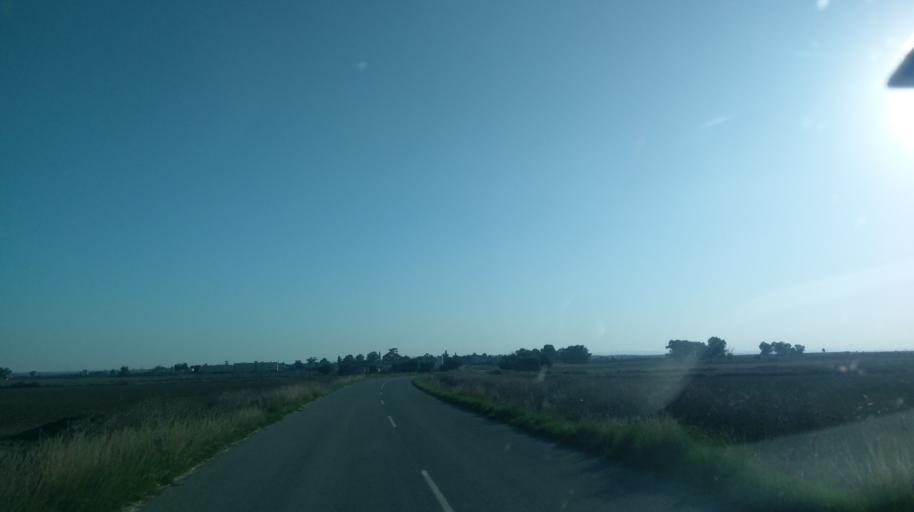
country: CY
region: Ammochostos
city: Lefkonoiko
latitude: 35.2631
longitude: 33.6867
